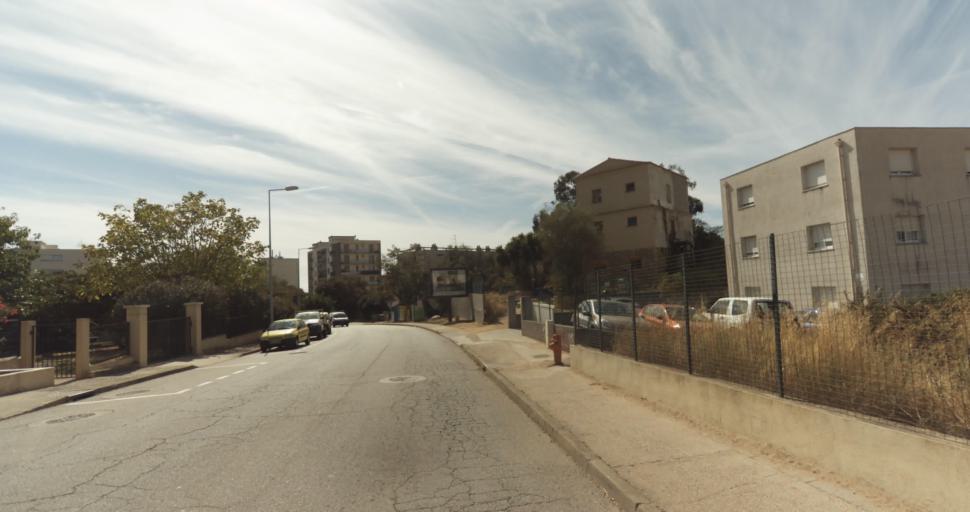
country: FR
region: Corsica
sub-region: Departement de la Corse-du-Sud
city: Ajaccio
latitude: 41.9366
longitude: 8.7568
